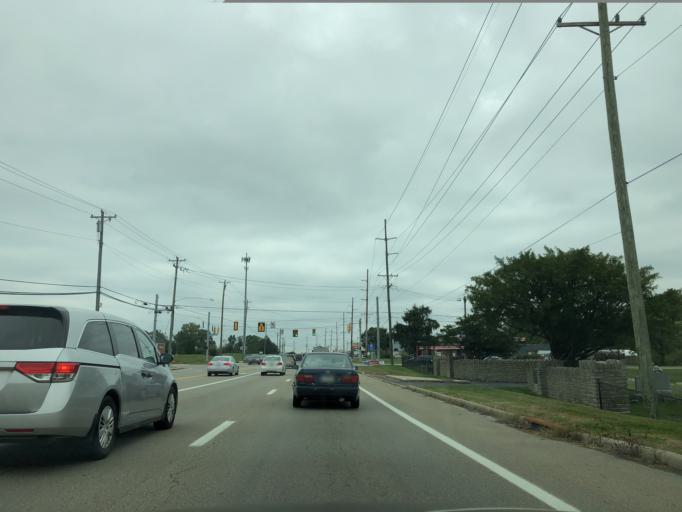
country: US
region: Ohio
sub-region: Hamilton County
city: Sixteen Mile Stand
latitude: 39.2871
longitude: -84.3062
